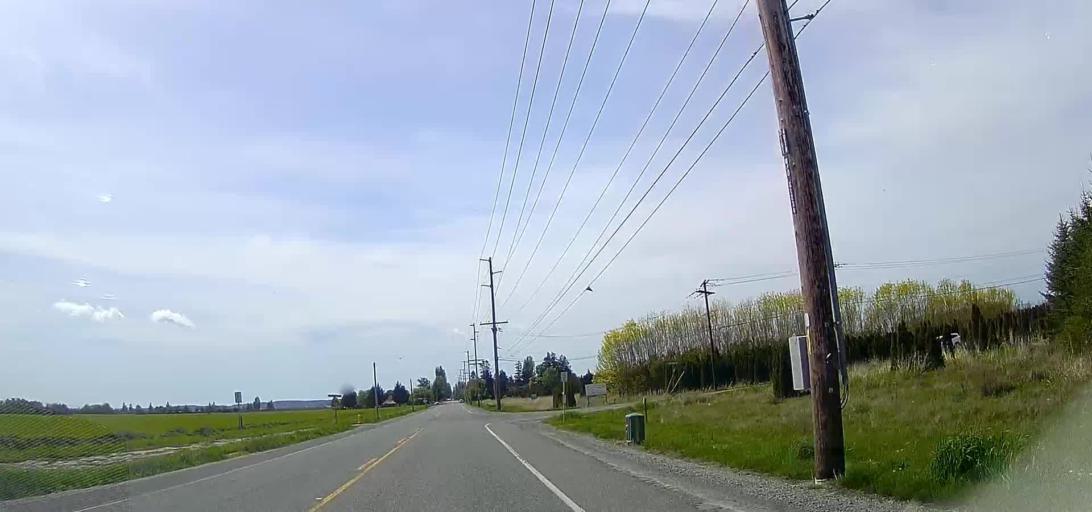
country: US
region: Washington
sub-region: Skagit County
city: Mount Vernon
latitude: 48.4209
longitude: -122.3780
